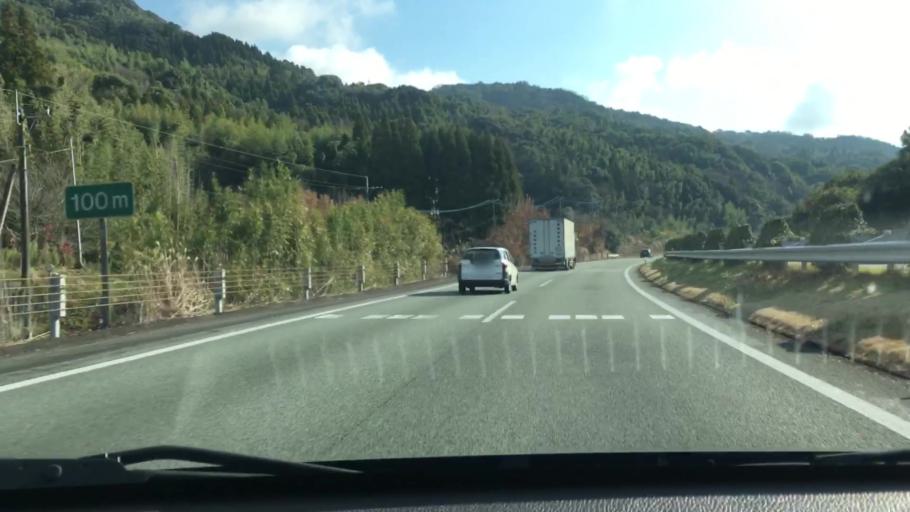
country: JP
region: Kumamoto
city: Matsubase
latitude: 32.6133
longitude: 130.7243
